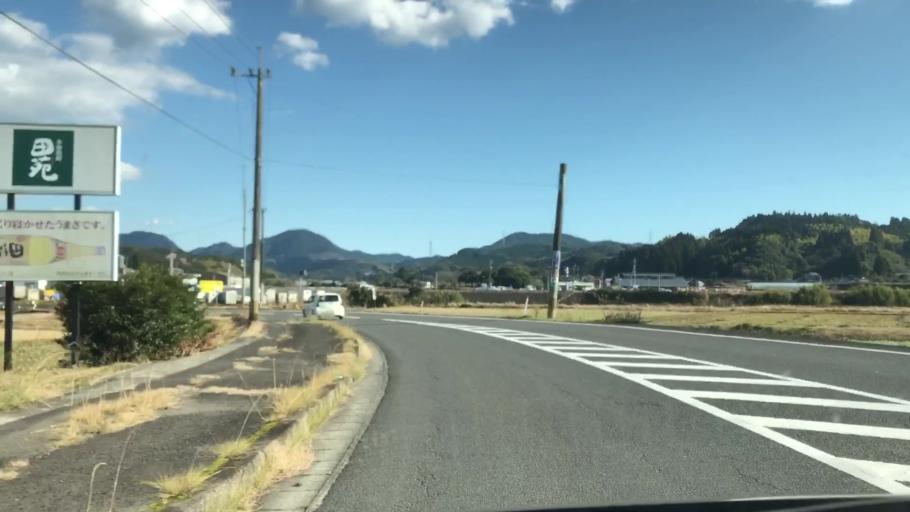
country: JP
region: Kagoshima
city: Satsumasendai
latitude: 31.7948
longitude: 130.4397
